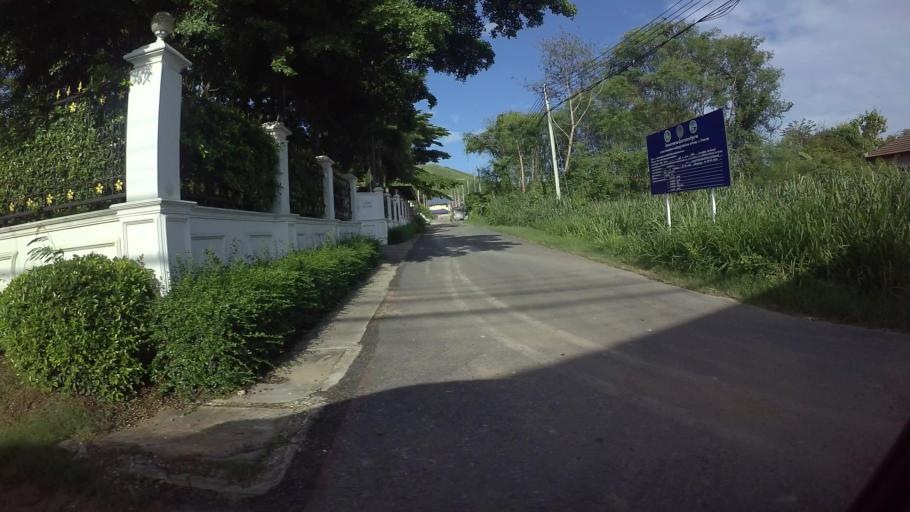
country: TH
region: Chon Buri
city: Sattahip
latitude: 12.6743
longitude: 100.9168
